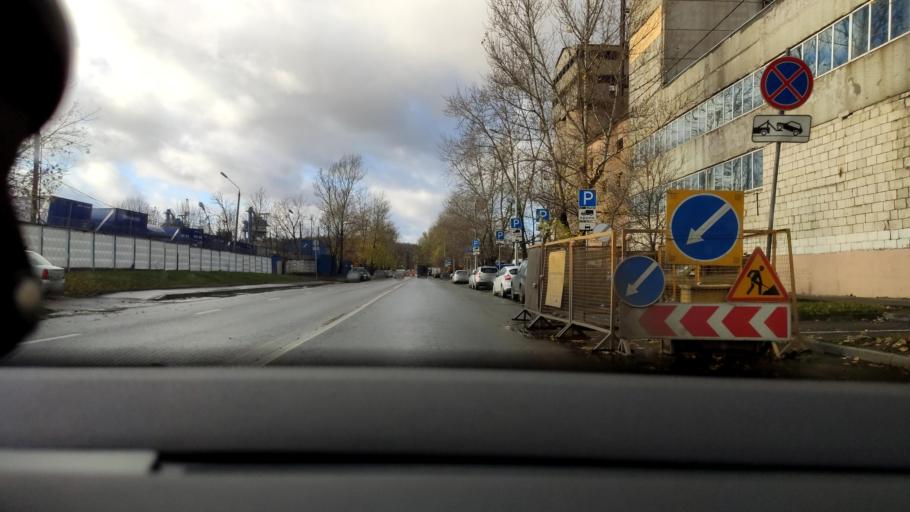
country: RU
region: Moscow
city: Vagonoremont
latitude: 55.8999
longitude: 37.5274
